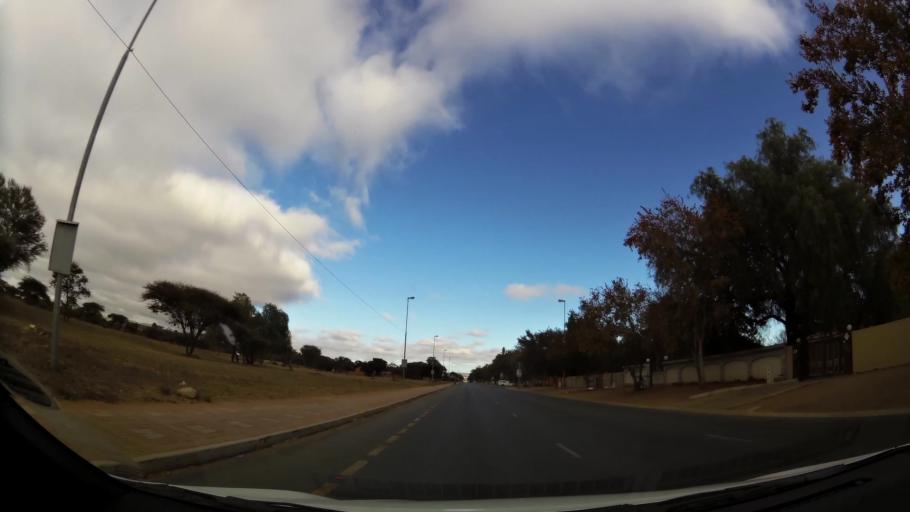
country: ZA
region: Limpopo
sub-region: Capricorn District Municipality
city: Polokwane
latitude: -23.9164
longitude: 29.4746
